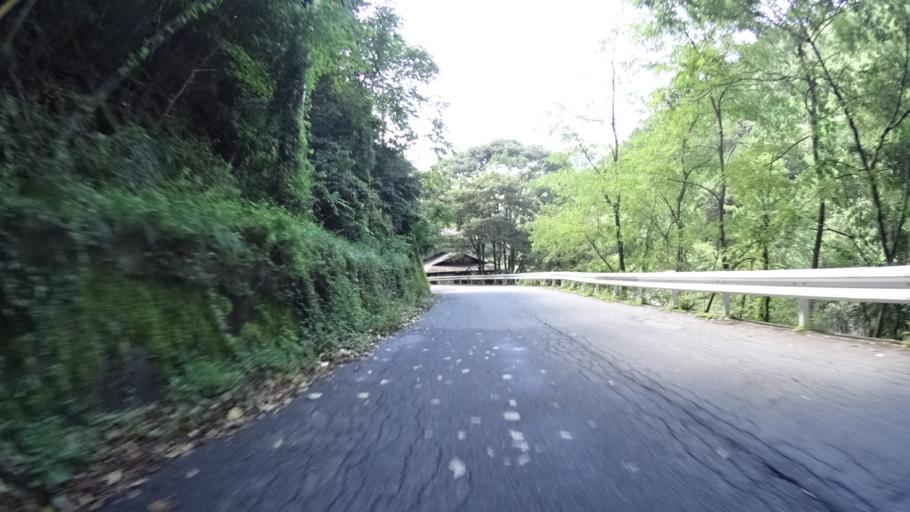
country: JP
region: Yamanashi
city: Enzan
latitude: 35.6517
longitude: 138.8162
